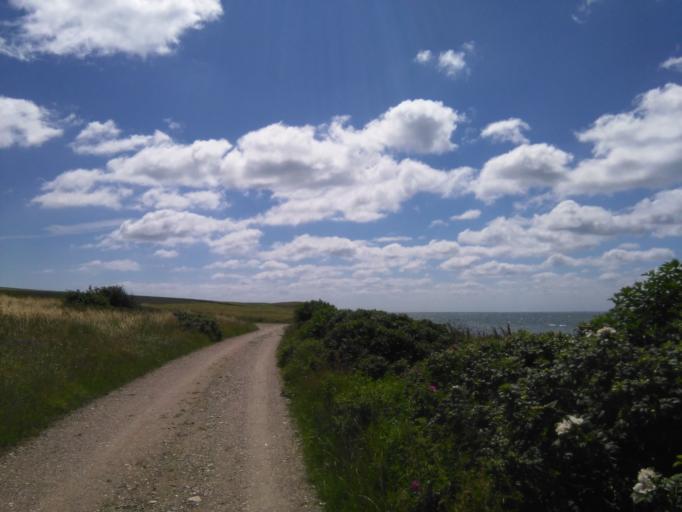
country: DK
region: Central Jutland
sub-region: Arhus Kommune
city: Logten
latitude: 56.1739
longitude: 10.3783
